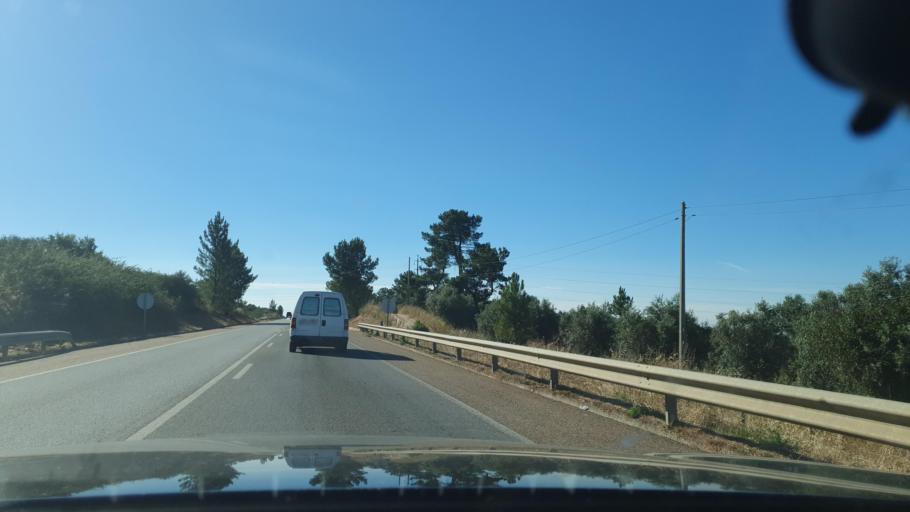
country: PT
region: Evora
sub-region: Borba
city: Borba
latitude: 38.7924
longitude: -7.4611
